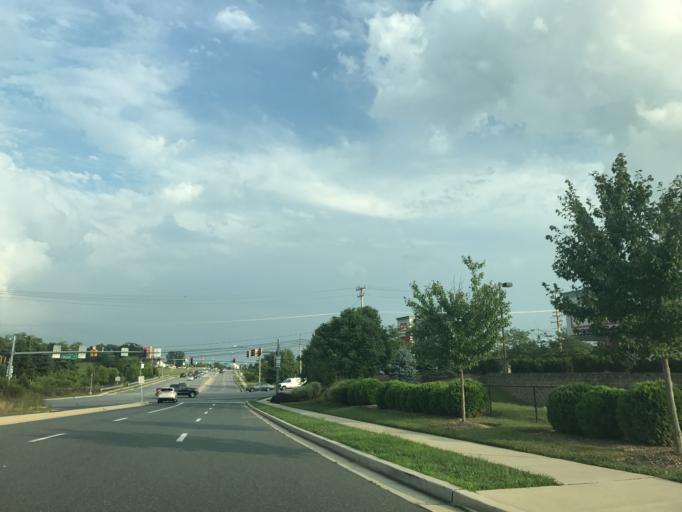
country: US
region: Maryland
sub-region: Baltimore County
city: Perry Hall
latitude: 39.4199
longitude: -76.4566
